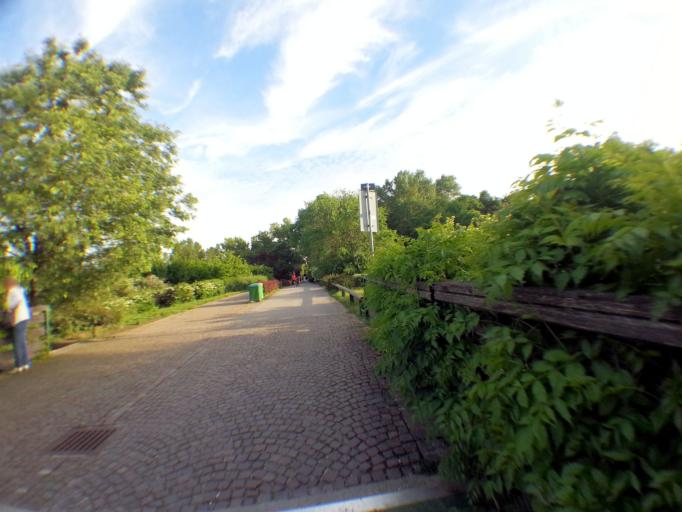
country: IT
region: Lombardy
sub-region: Citta metropolitana di Milano
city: Bresso
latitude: 45.5332
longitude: 9.2113
